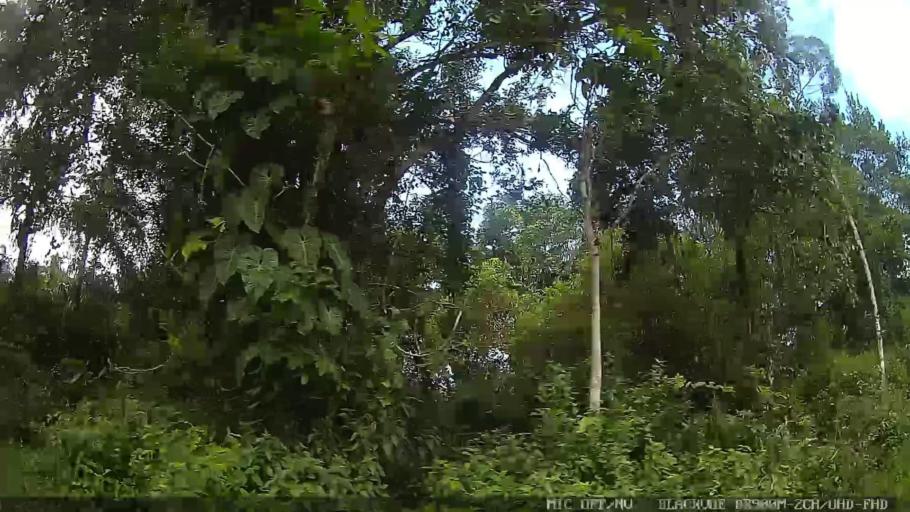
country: BR
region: Sao Paulo
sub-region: Itanhaem
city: Itanhaem
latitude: -24.1758
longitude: -46.9326
